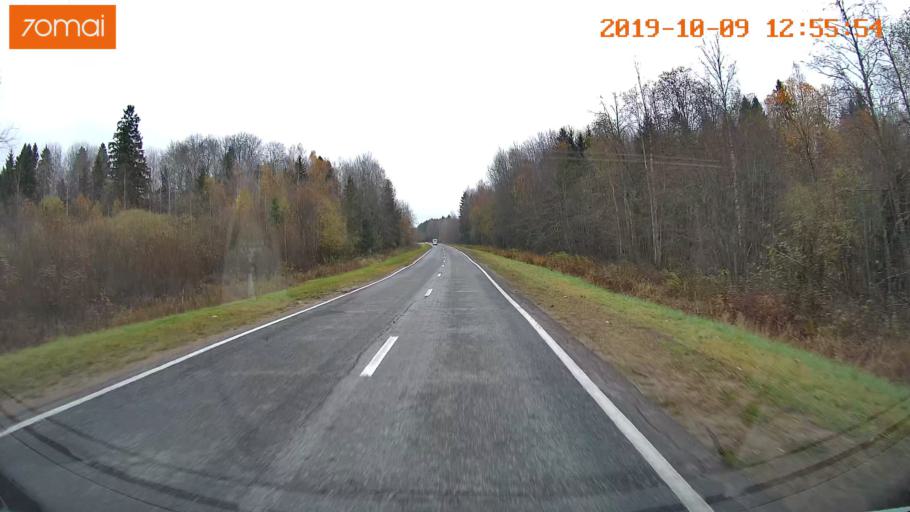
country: RU
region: Jaroslavl
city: Prechistoye
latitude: 58.3969
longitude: 40.4048
